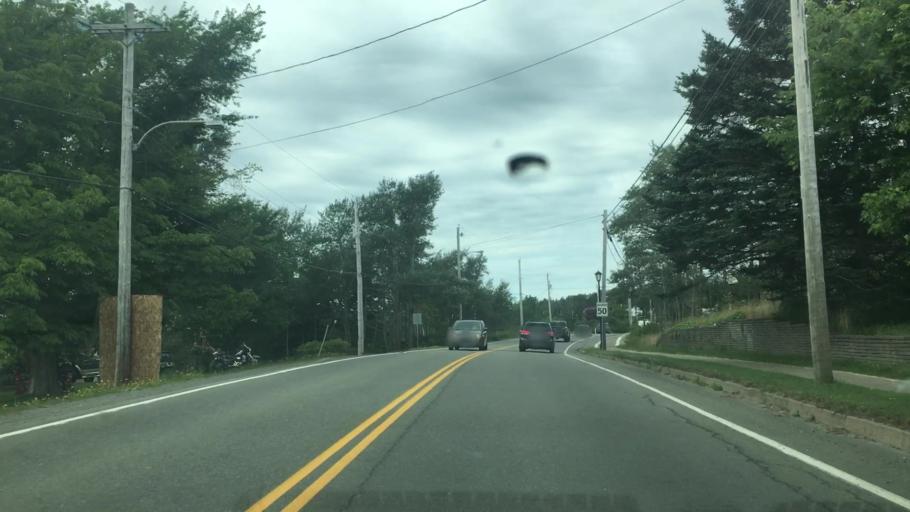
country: CA
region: Nova Scotia
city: Princeville
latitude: 45.6558
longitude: -60.8828
